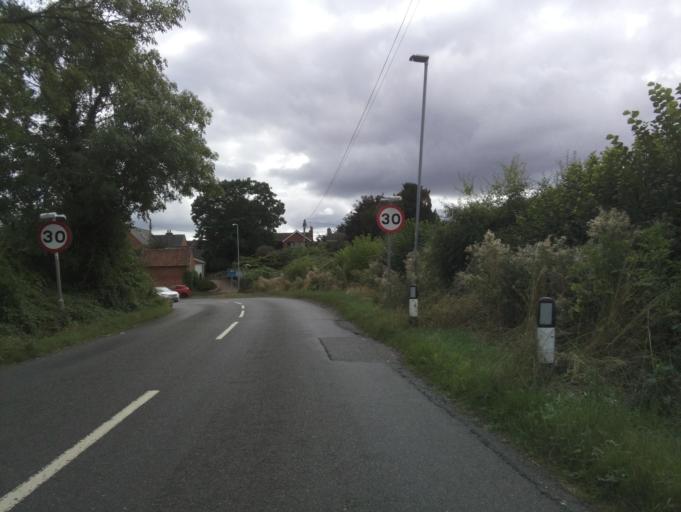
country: GB
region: England
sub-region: Leicestershire
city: Loughborough
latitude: 52.7959
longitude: -1.1982
